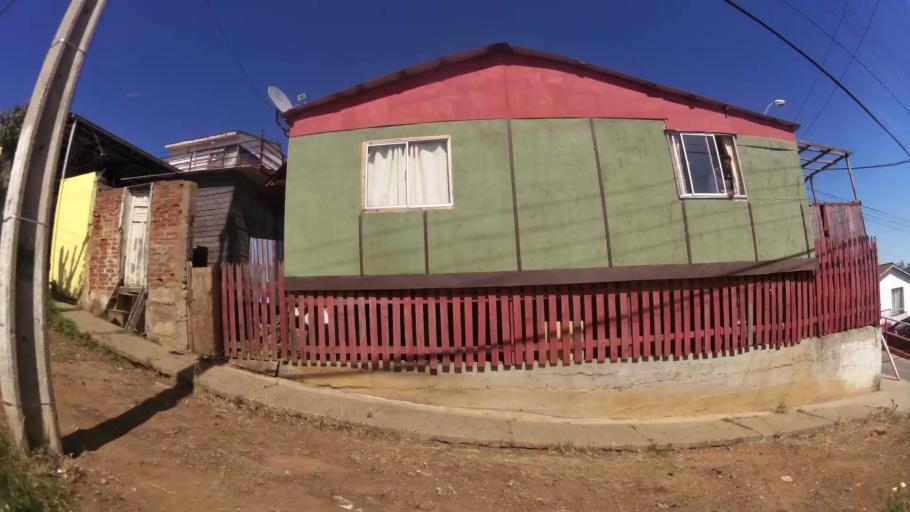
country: CL
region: Valparaiso
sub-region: Provincia de Valparaiso
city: Valparaiso
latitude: -33.0463
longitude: -71.6473
